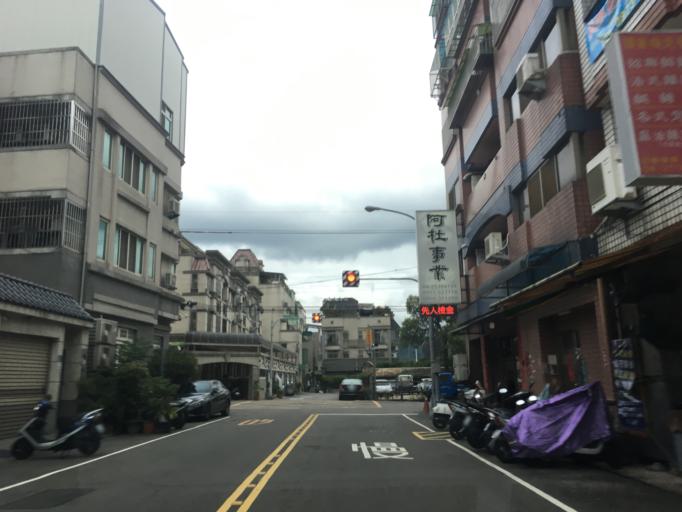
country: TW
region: Taiwan
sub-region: Taichung City
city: Taichung
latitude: 24.1945
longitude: 120.7043
